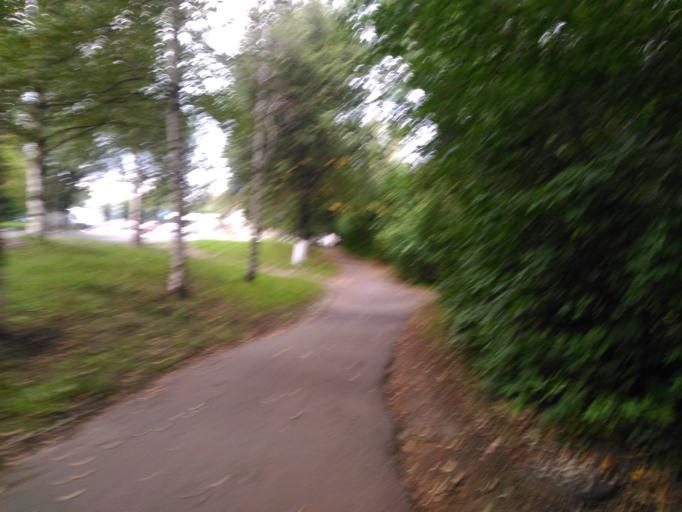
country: RU
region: Ulyanovsk
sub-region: Ulyanovskiy Rayon
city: Ulyanovsk
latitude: 54.2708
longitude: 48.3350
